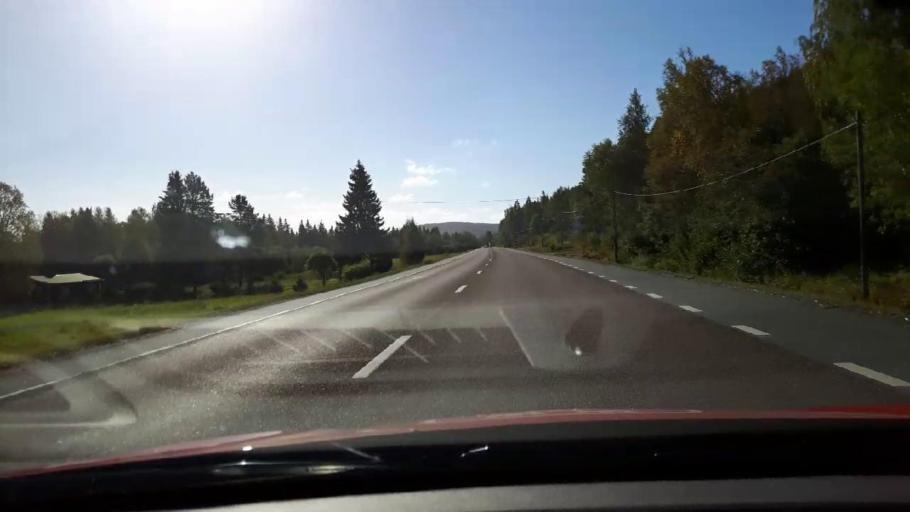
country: SE
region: Jaemtland
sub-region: Braecke Kommun
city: Braecke
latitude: 62.9253
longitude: 15.2272
